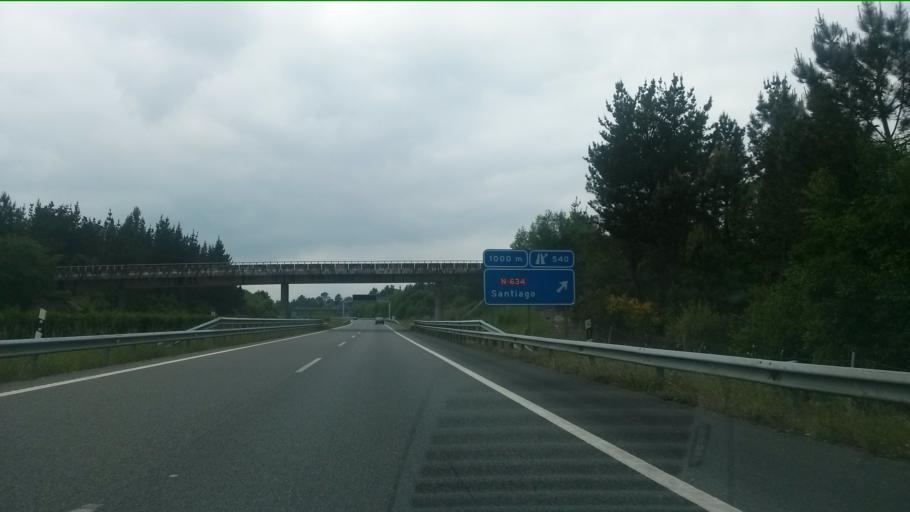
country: ES
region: Galicia
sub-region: Provincia de Lugo
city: Guitiriz
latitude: 43.1895
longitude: -7.9338
